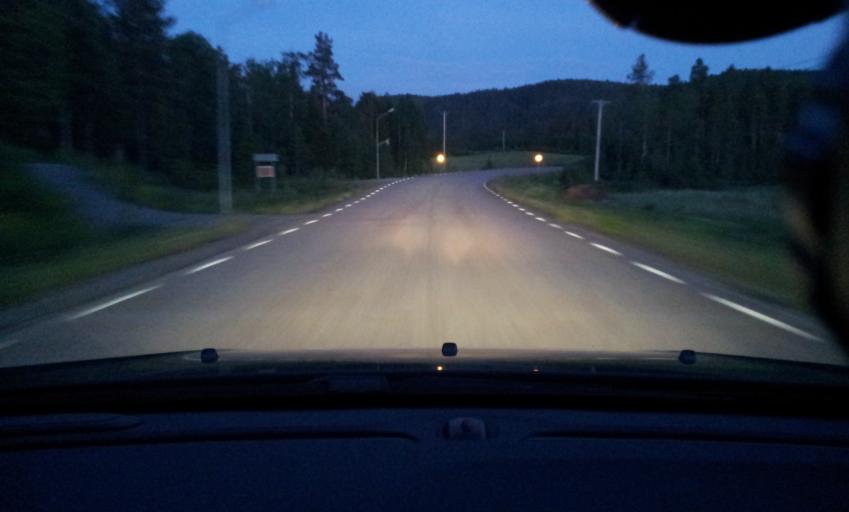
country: SE
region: Jaemtland
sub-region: Bergs Kommun
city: Hoverberg
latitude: 62.6613
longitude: 14.7461
